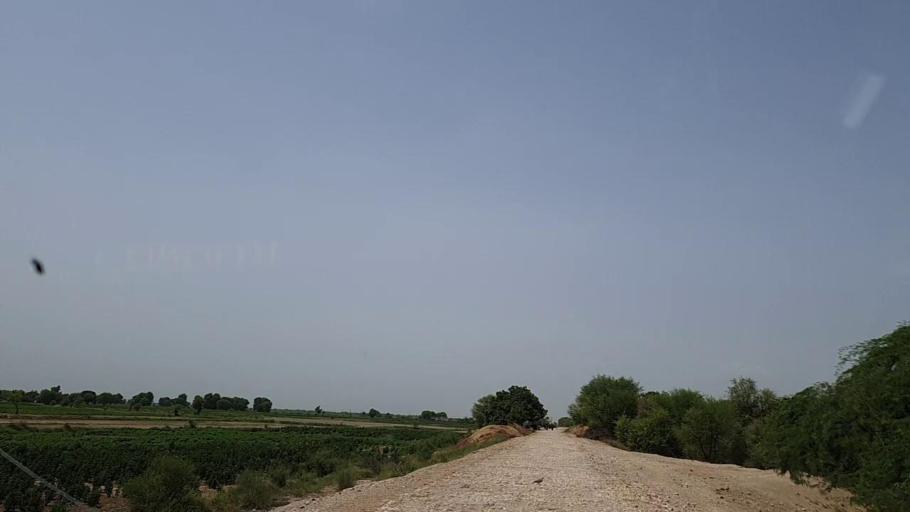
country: PK
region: Sindh
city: Tharu Shah
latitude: 27.0353
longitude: 68.1115
